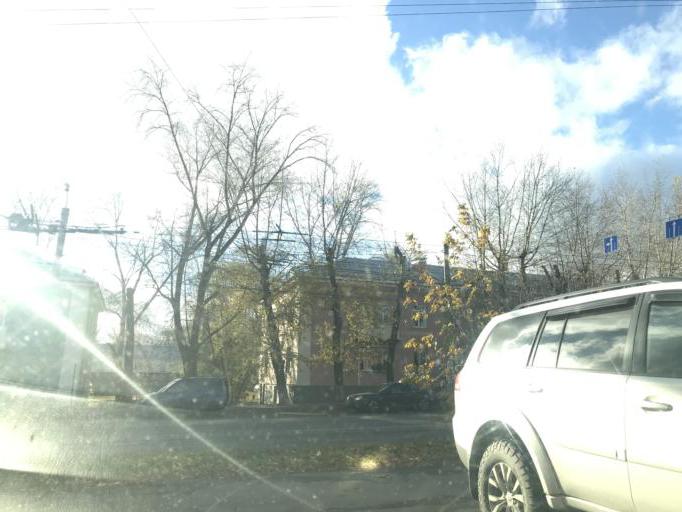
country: RU
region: Chelyabinsk
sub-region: Gorod Chelyabinsk
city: Chelyabinsk
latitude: 55.1807
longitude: 61.4466
